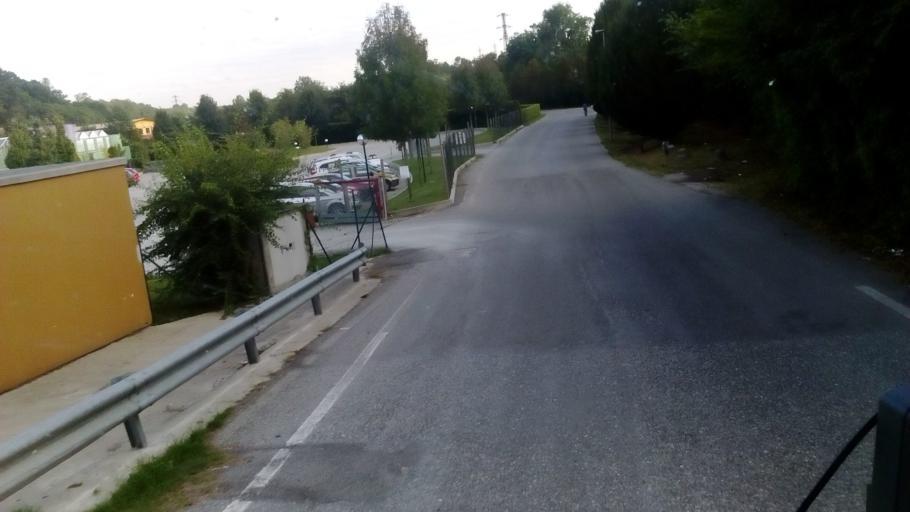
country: IT
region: Lombardy
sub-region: Provincia di Como
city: Novedrate
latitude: 45.6948
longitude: 9.1170
